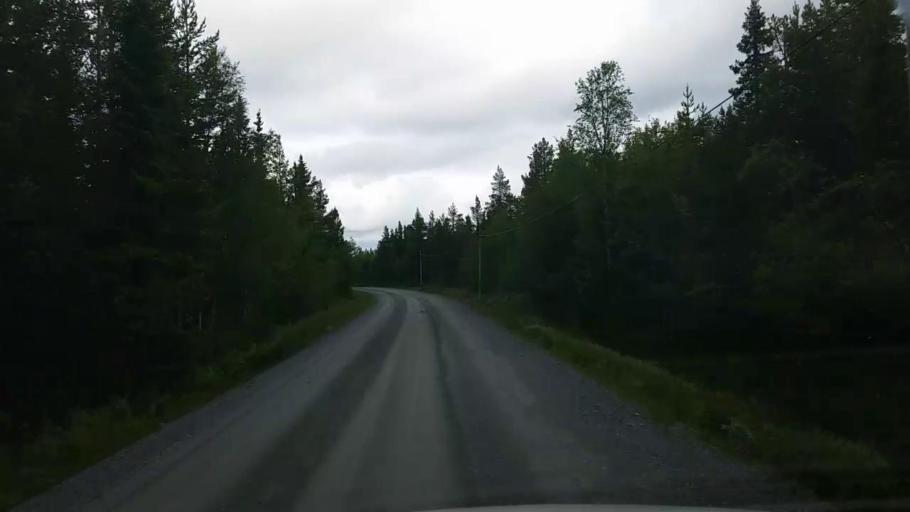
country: NO
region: Hedmark
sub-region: Engerdal
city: Engerdal
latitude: 62.4060
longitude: 12.6660
